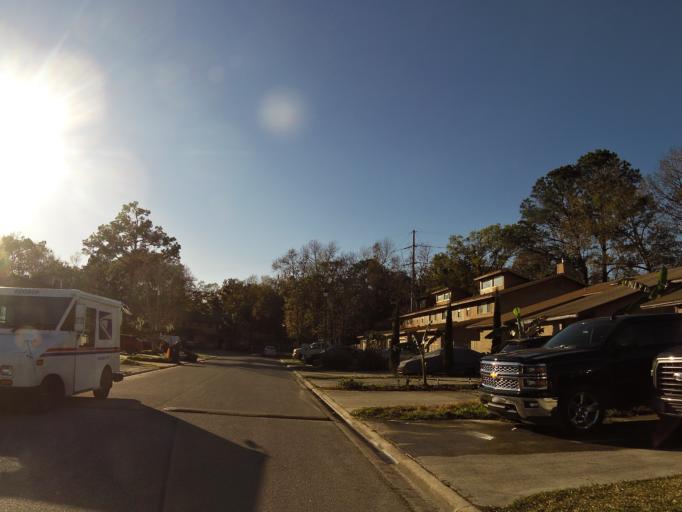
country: US
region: Florida
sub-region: Duval County
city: Jacksonville
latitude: 30.2291
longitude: -81.5988
